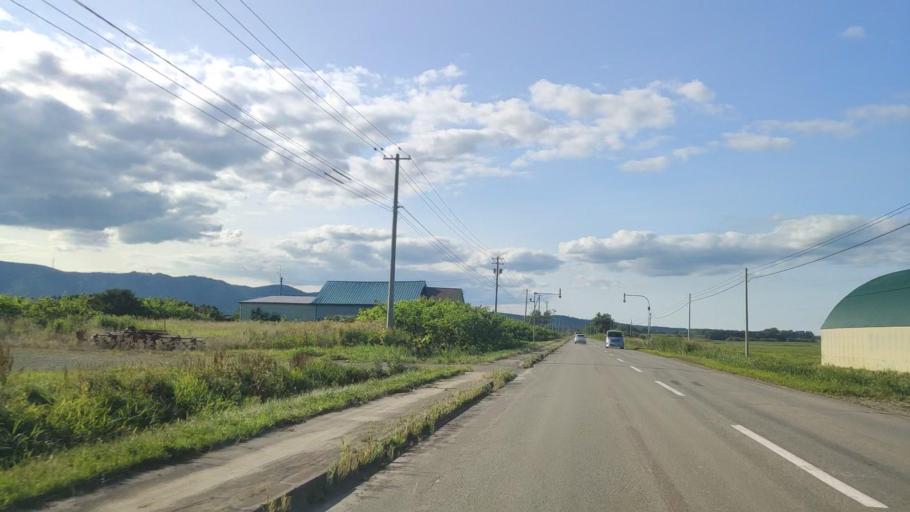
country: JP
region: Hokkaido
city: Makubetsu
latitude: 44.8246
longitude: 142.0643
